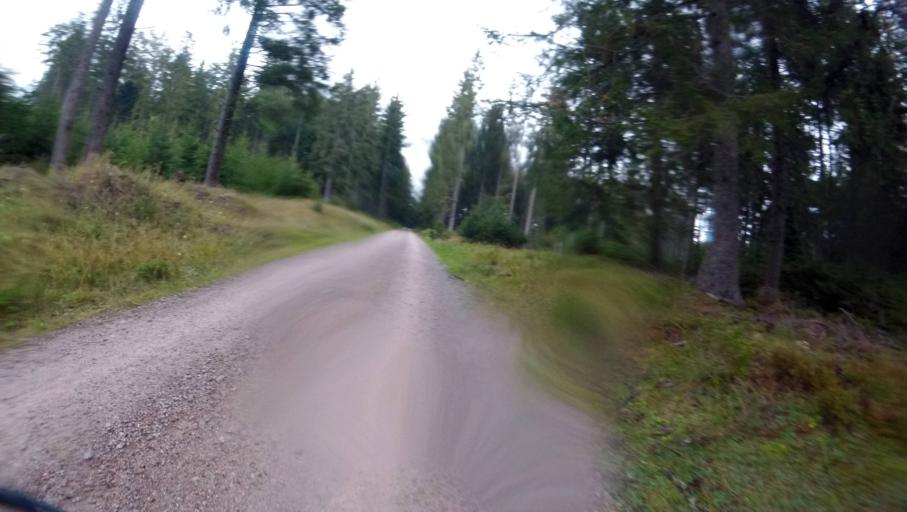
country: DE
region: Baden-Wuerttemberg
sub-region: Karlsruhe Region
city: Weisenbach
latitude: 48.7018
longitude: 8.4073
